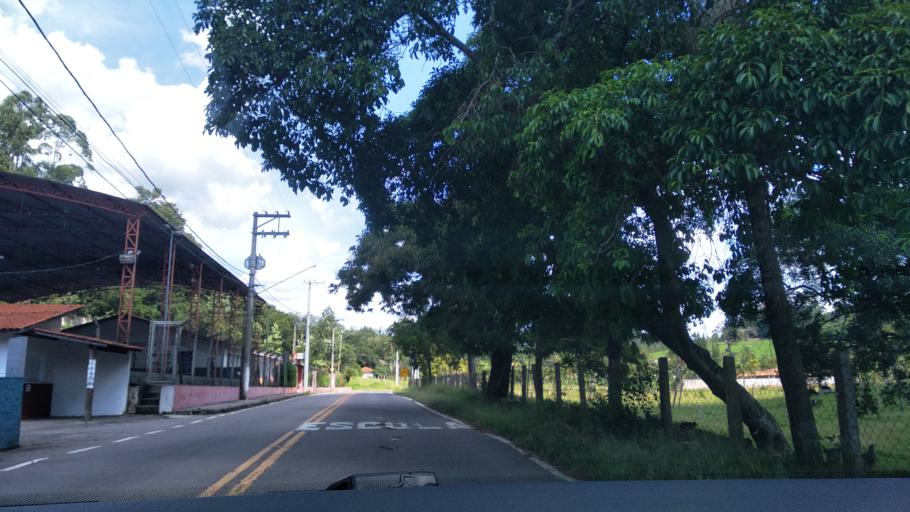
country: BR
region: Sao Paulo
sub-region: Varzea Paulista
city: Varzea Paulista
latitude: -23.2620
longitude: -46.8830
